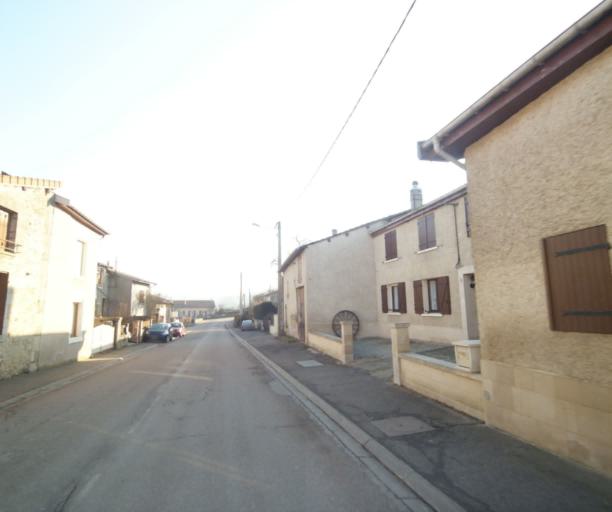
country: FR
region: Champagne-Ardenne
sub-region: Departement de la Haute-Marne
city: Bienville
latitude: 48.5816
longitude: 5.0883
